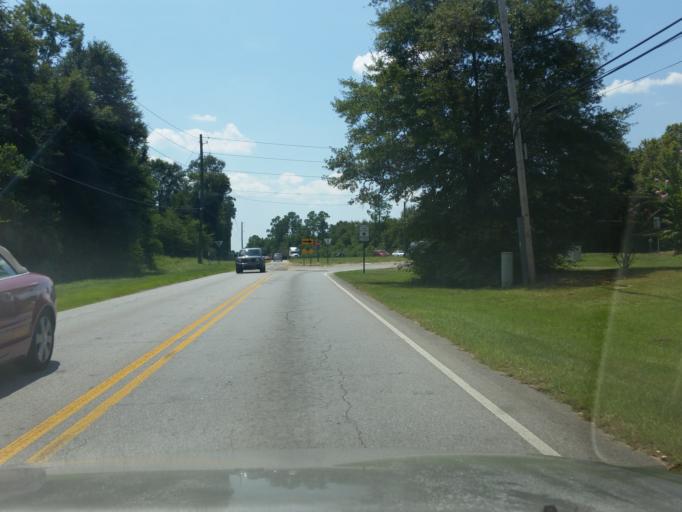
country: US
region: Florida
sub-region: Escambia County
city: Cantonment
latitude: 30.6162
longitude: -87.3229
